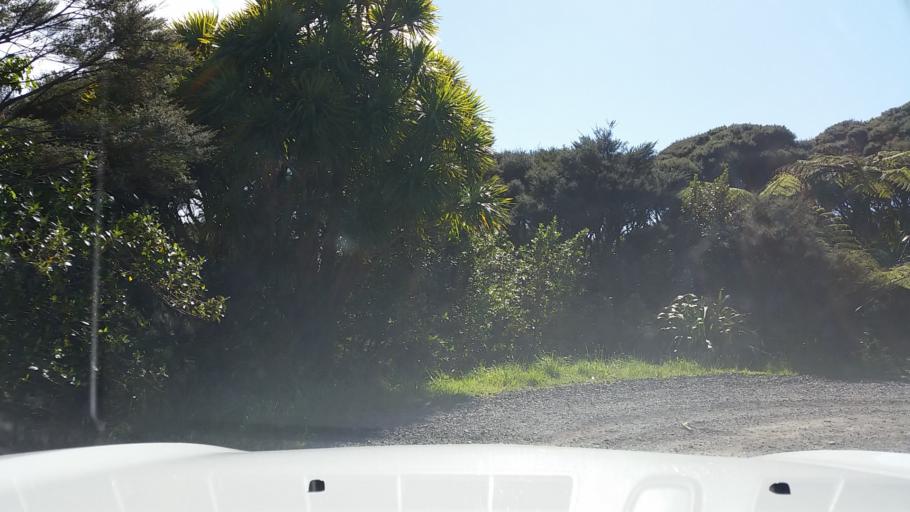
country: NZ
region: Auckland
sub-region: Auckland
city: Titirangi
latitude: -37.0144
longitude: 174.5379
